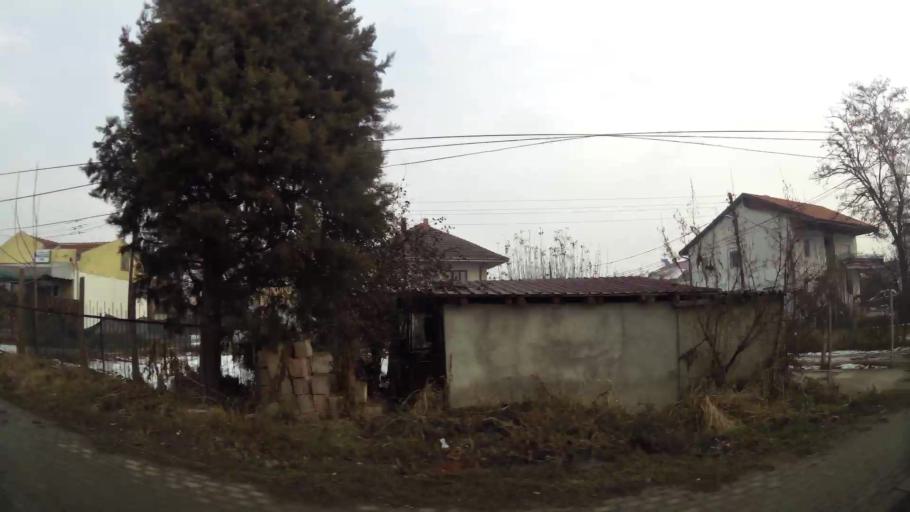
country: MK
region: Ilinden
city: Jurumleri
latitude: 41.9827
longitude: 21.5241
